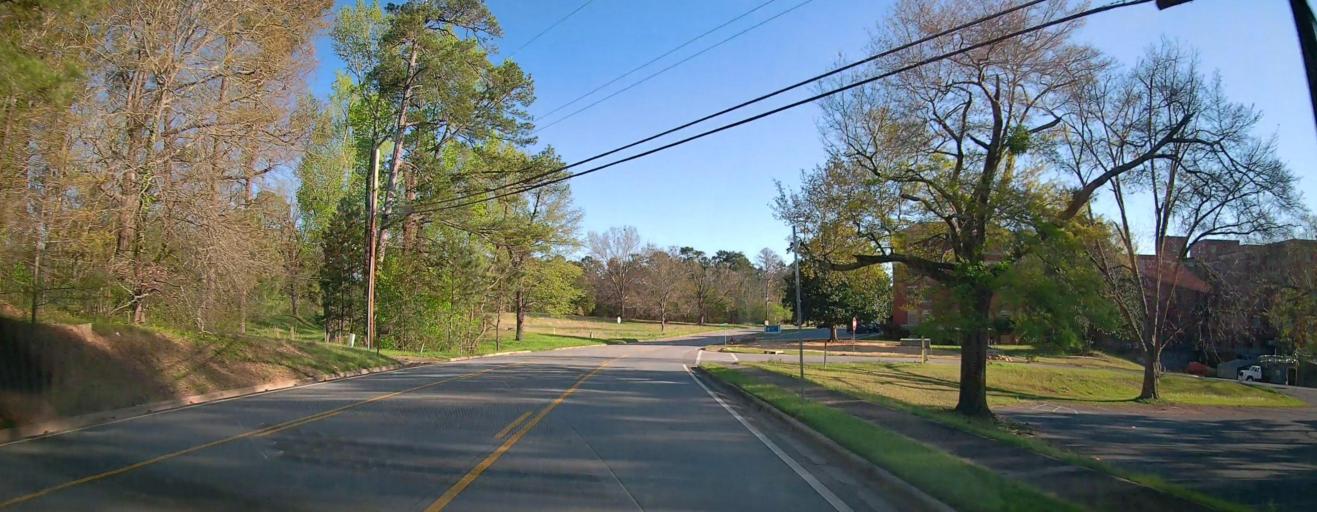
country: US
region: Georgia
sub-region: Baldwin County
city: Hardwick
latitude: 33.0479
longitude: -83.2128
